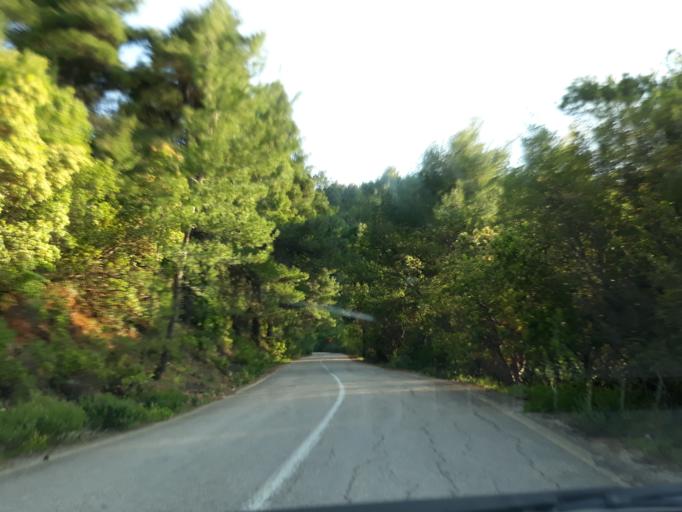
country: GR
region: Attica
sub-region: Nomarchia Anatolikis Attikis
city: Afidnes
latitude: 38.2228
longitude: 23.7845
